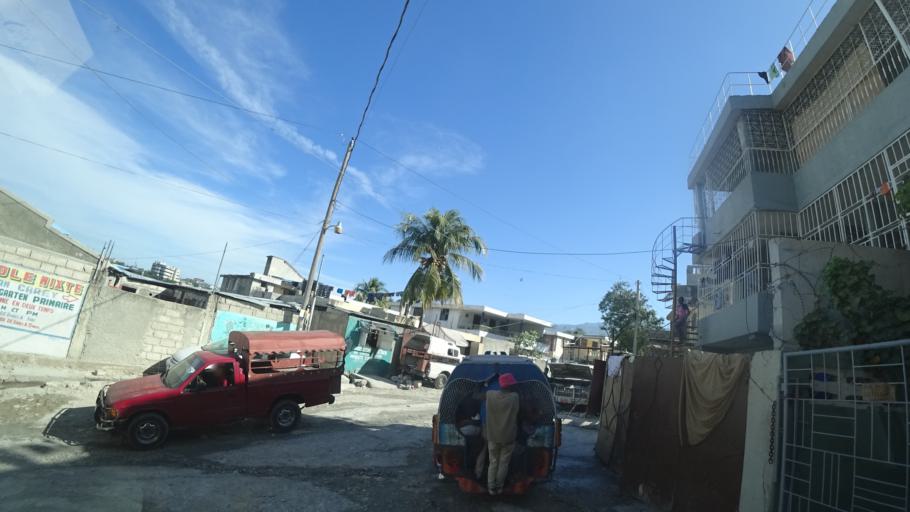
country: HT
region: Ouest
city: Delmas 73
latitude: 18.5500
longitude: -72.3155
